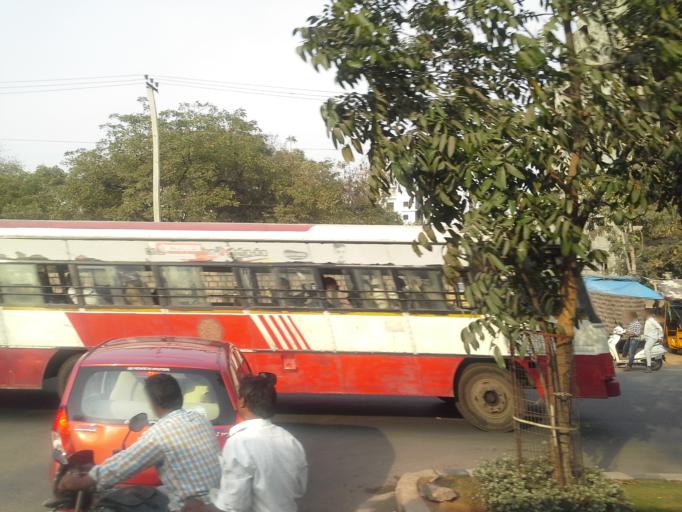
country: IN
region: Telangana
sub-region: Rangareddi
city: Kukatpalli
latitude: 17.4420
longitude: 78.3581
